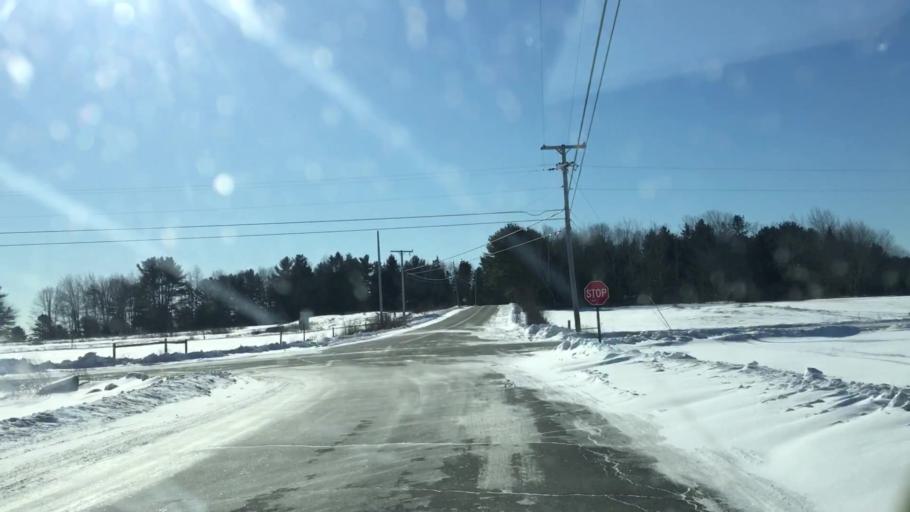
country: US
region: Maine
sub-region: Cumberland County
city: Brunswick
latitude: 43.8911
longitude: -69.9988
